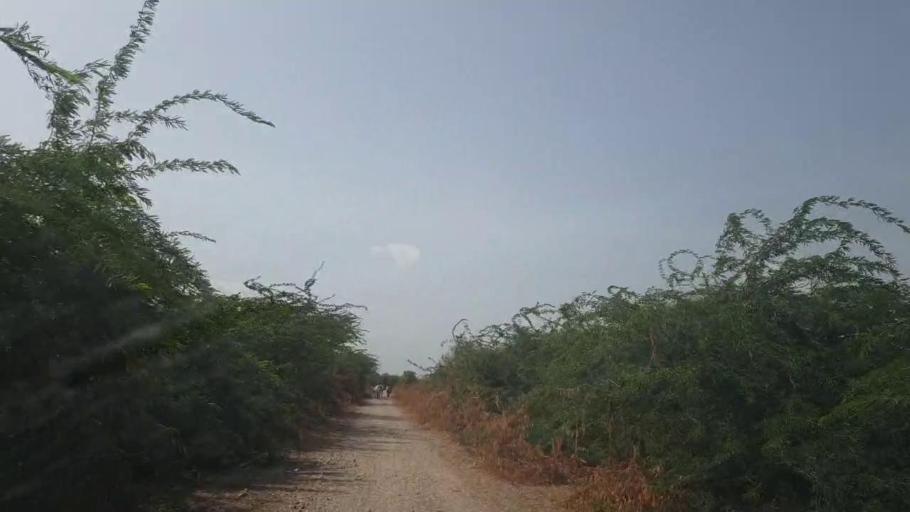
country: PK
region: Sindh
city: Tando Bago
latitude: 24.7787
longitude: 69.1305
